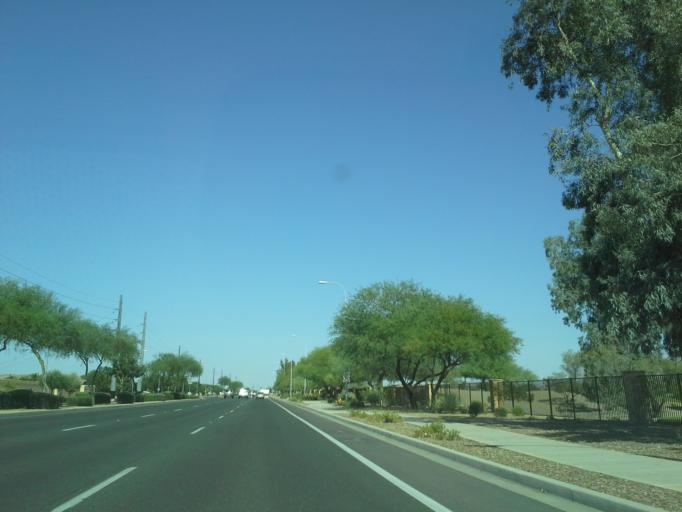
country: US
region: Arizona
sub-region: Maricopa County
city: Sun Lakes
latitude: 33.2191
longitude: -111.7794
